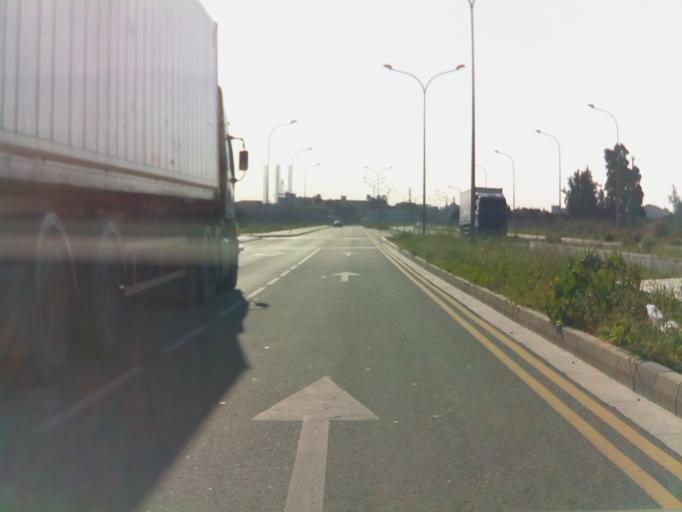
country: CY
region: Limassol
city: Ypsonas
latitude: 34.6616
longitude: 32.9941
